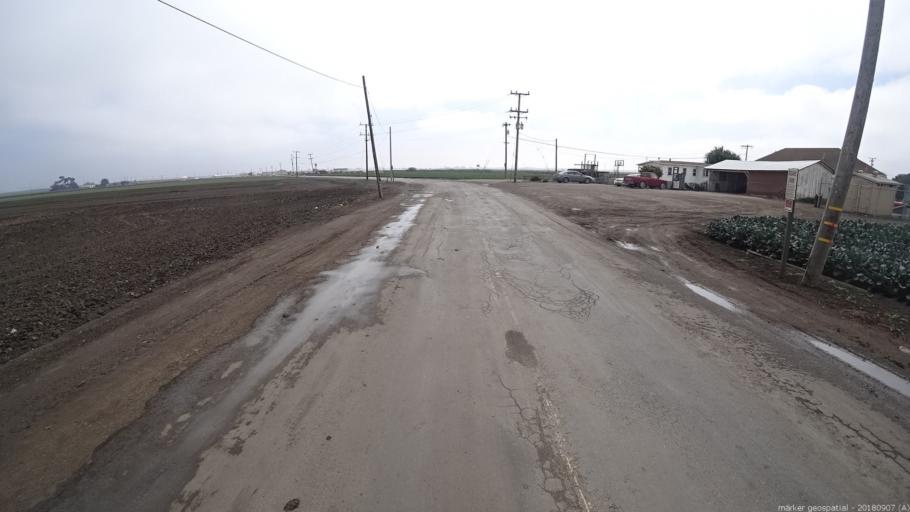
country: US
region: California
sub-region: Monterey County
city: Boronda
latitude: 36.6922
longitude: -121.7084
